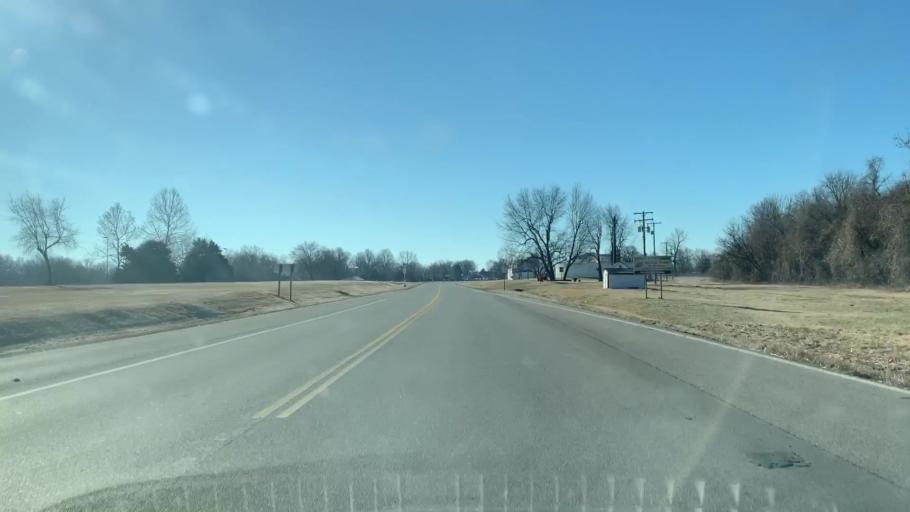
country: US
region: Kansas
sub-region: Cherokee County
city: Baxter Springs
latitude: 37.0376
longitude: -94.7352
